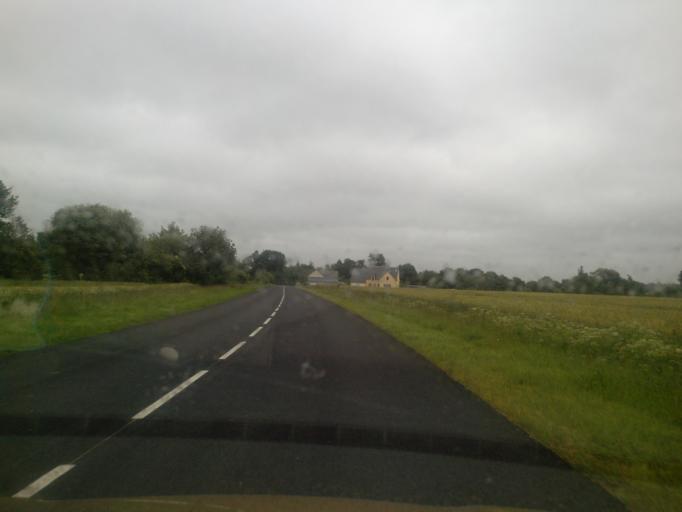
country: FR
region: Brittany
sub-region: Departement d'Ille-et-Vilaine
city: Sens-de-Bretagne
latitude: 48.3401
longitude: -1.4995
